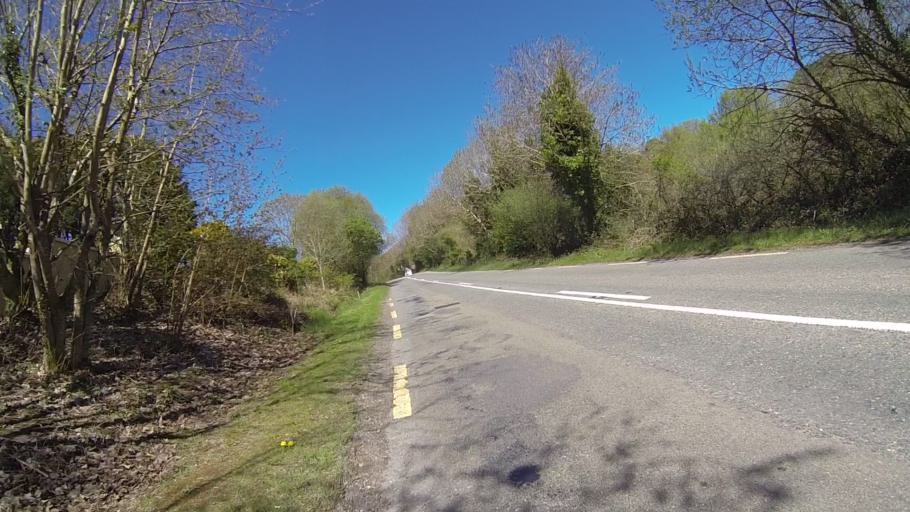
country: IE
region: Munster
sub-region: Ciarrai
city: Kenmare
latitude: 51.8923
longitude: -9.5999
